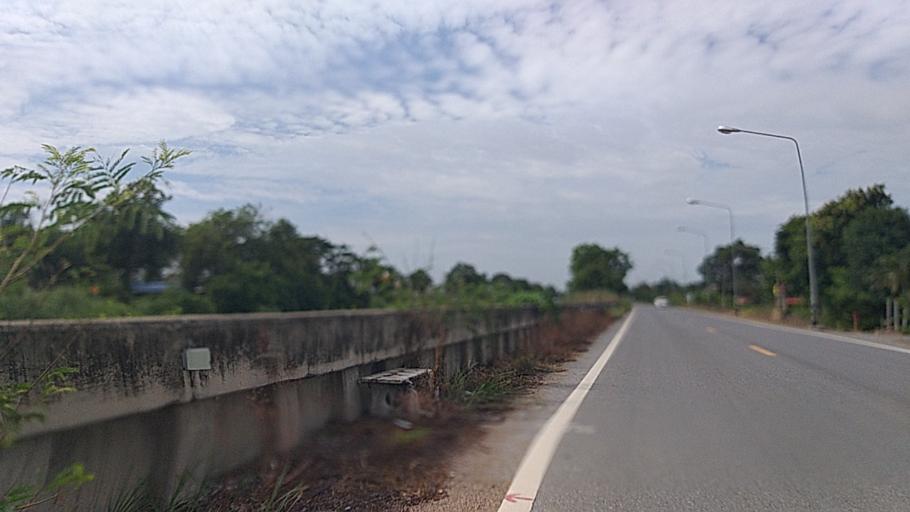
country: TH
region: Pathum Thani
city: Nong Suea
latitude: 14.0372
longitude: 100.8932
